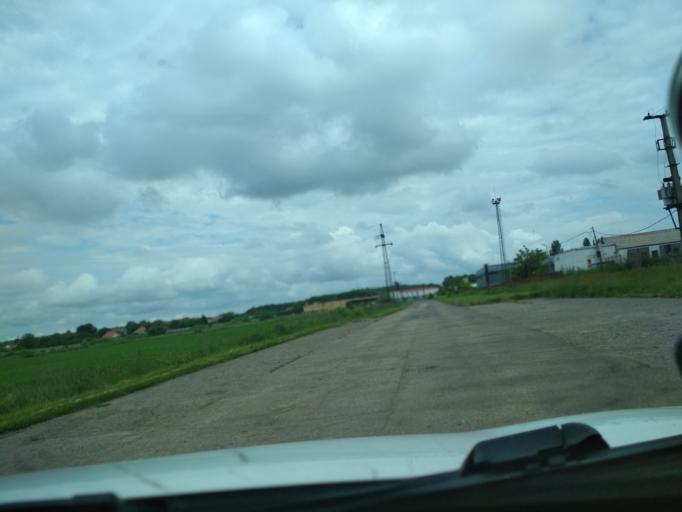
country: HU
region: Jasz-Nagykun-Szolnok
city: Tiszafured
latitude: 47.6059
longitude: 20.7329
